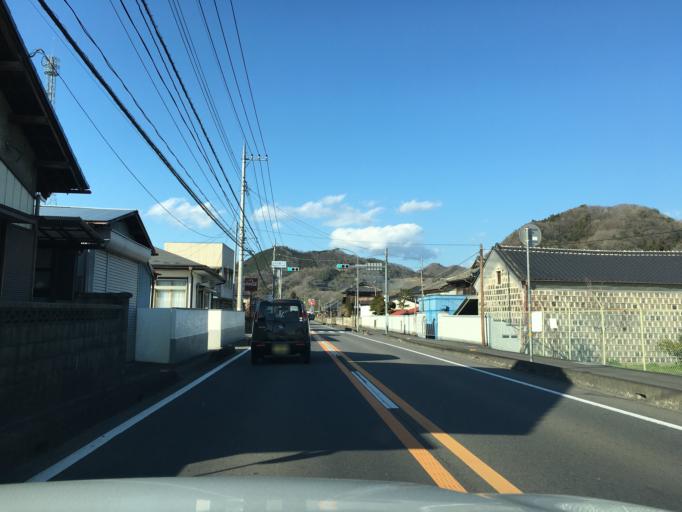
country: JP
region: Ibaraki
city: Omiya
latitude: 36.6455
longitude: 140.3926
